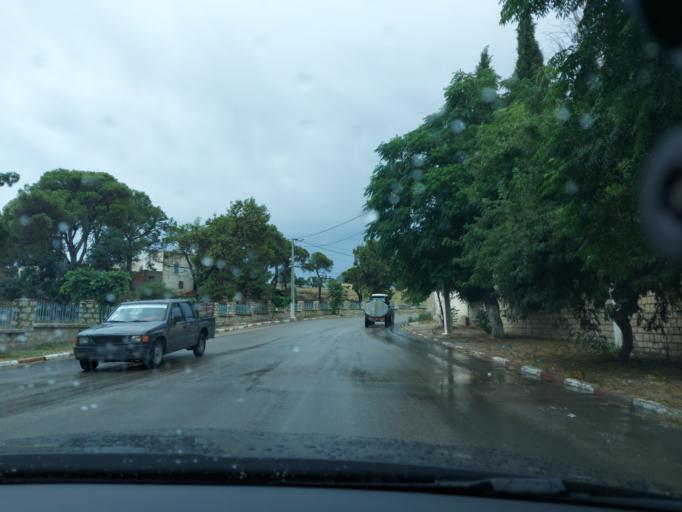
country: TN
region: Silyanah
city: Maktar
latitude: 35.8557
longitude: 9.2048
